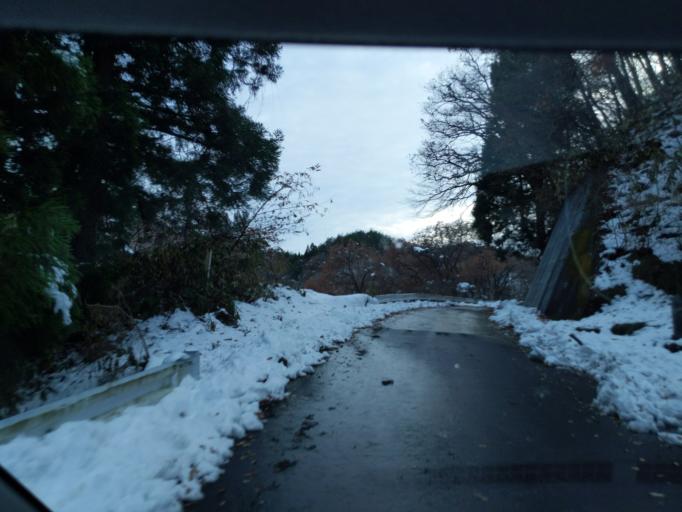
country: JP
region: Iwate
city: Mizusawa
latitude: 39.0413
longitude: 141.0368
